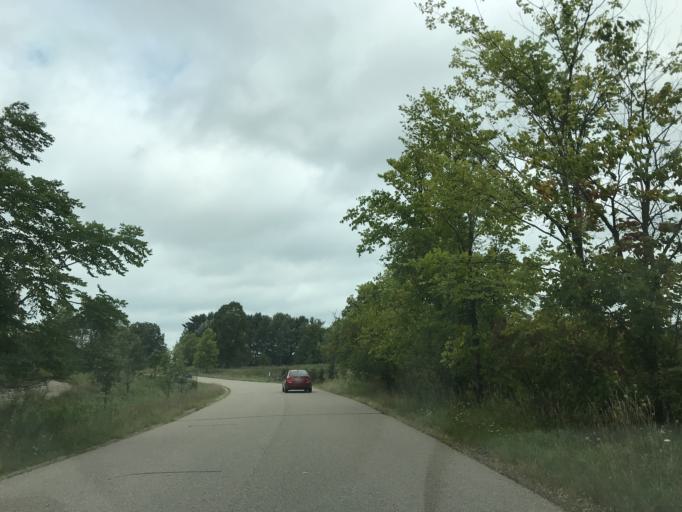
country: US
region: Michigan
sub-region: Washtenaw County
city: Ypsilanti
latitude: 42.3007
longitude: -83.6614
